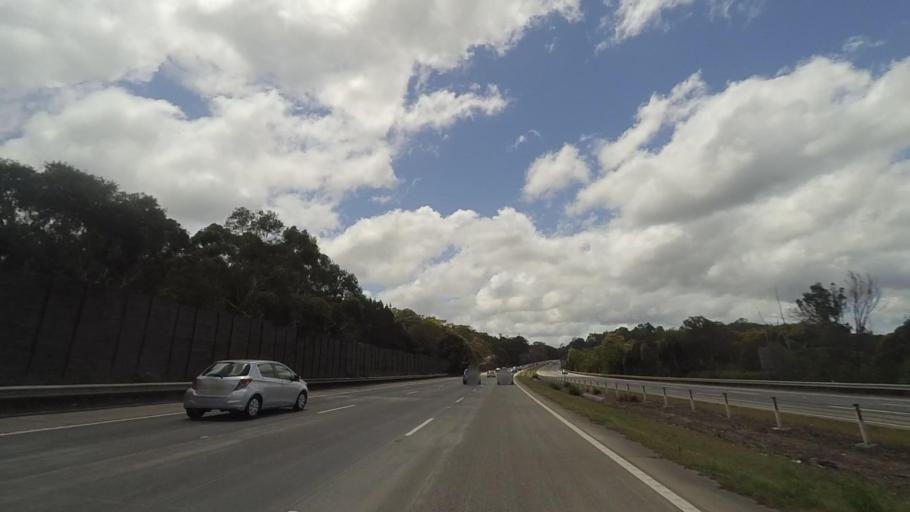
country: AU
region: New South Wales
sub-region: Hornsby Shire
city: Mount Colah
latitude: -33.6699
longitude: 151.1209
